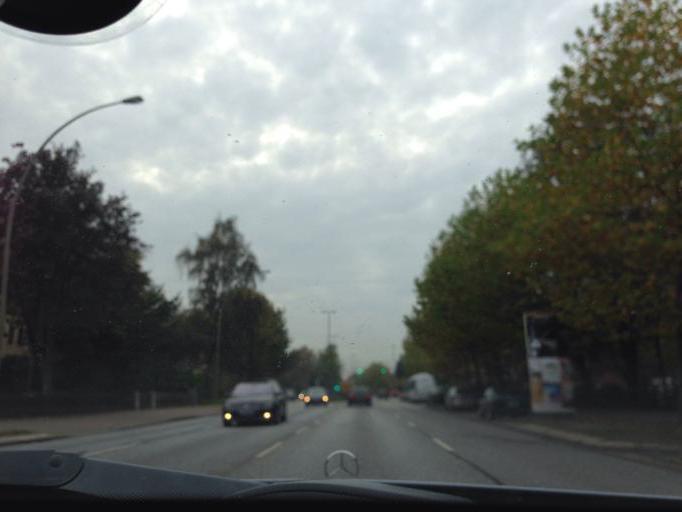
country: DE
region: Hamburg
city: Farmsen-Berne
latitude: 53.5892
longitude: 10.1263
